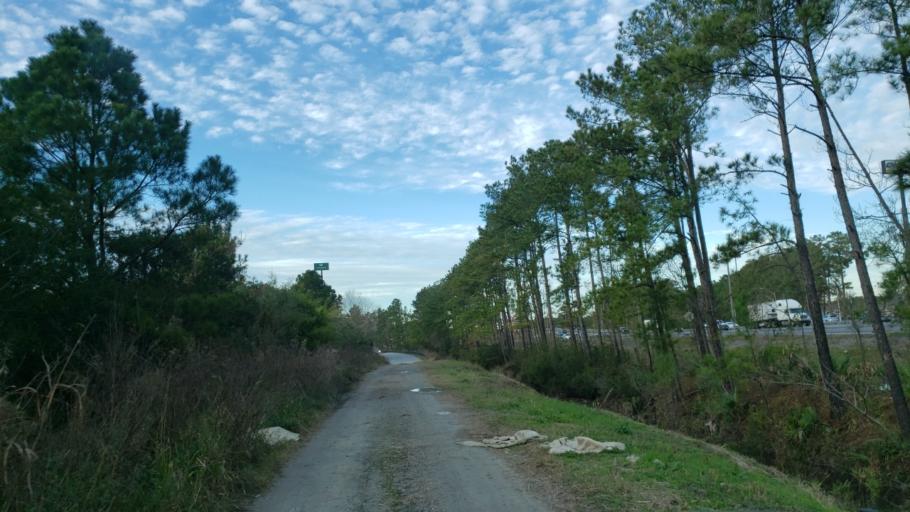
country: US
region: Georgia
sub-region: Chatham County
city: Pooler
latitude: 32.1071
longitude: -81.2382
